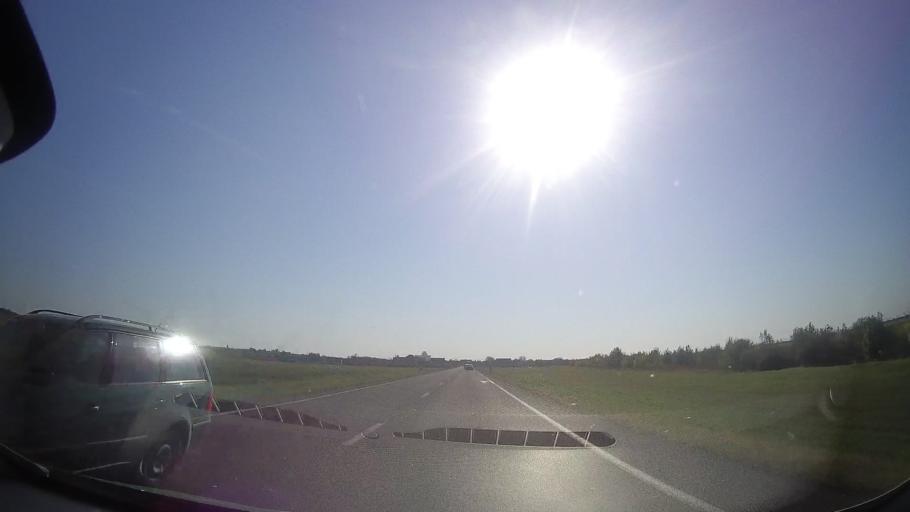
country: RO
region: Timis
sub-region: Comuna Topolovatu Mare
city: Topolovatu Mare
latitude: 45.7795
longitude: 21.6084
